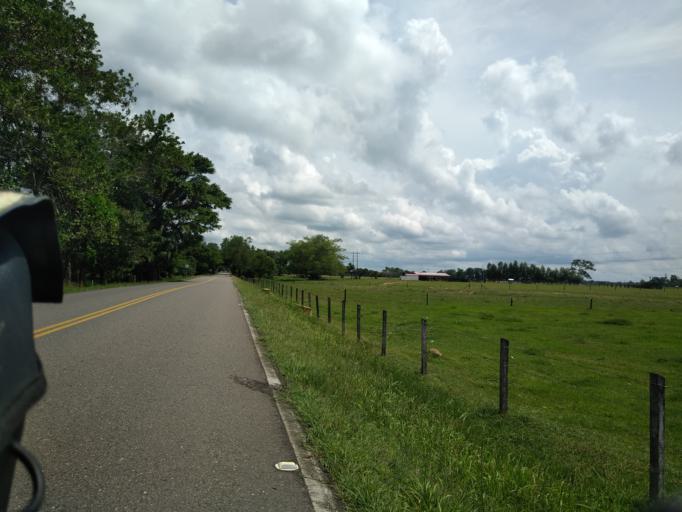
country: CO
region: Santander
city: Puerto Parra
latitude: 6.5027
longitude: -74.0576
